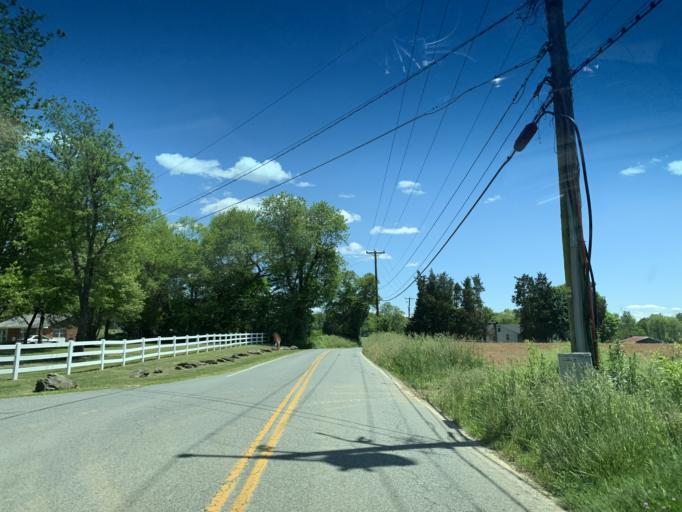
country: US
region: Maryland
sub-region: Cecil County
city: Charlestown
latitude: 39.6413
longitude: -76.0109
